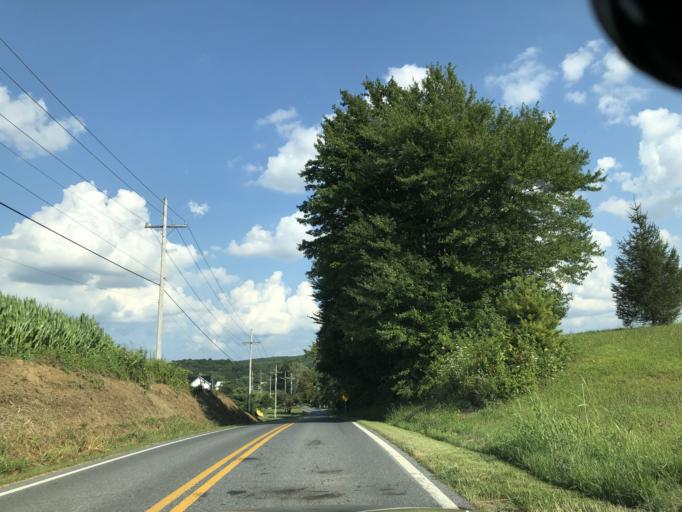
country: US
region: Maryland
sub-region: Frederick County
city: Linganore
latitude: 39.4713
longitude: -77.1789
